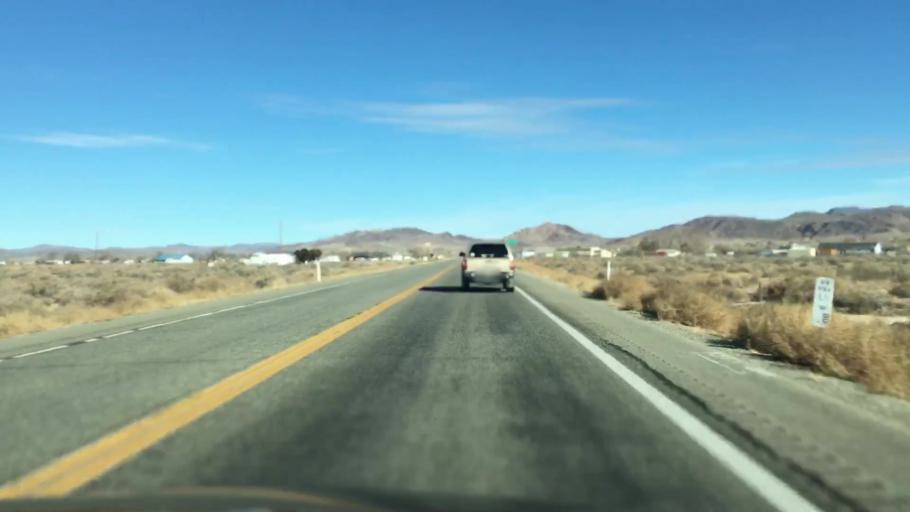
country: US
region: Nevada
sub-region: Lyon County
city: Yerington
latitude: 39.0076
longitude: -119.0832
